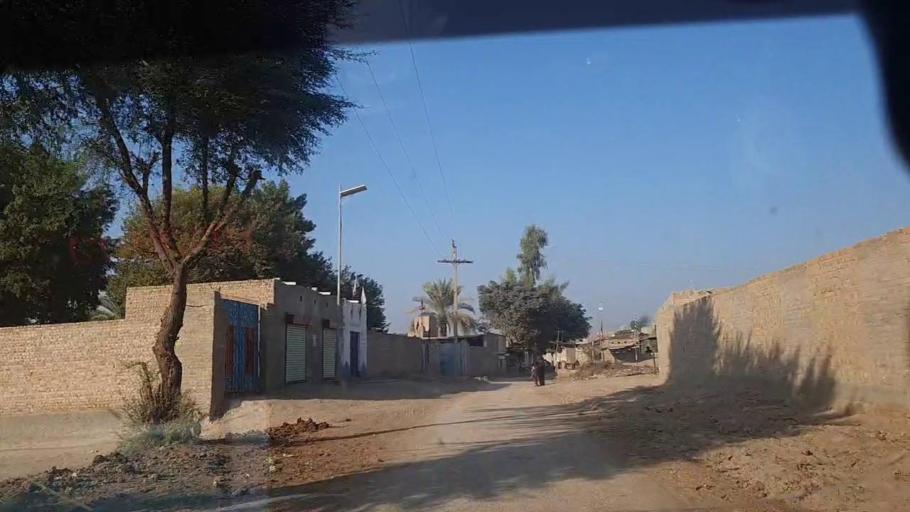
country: PK
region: Sindh
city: Sobhadero
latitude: 27.2552
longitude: 68.3508
